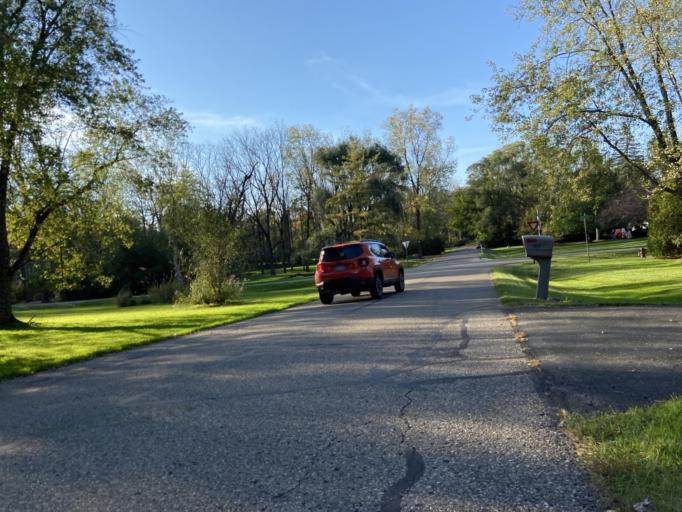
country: US
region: Michigan
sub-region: Oakland County
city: Franklin
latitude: 42.5094
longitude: -83.3308
